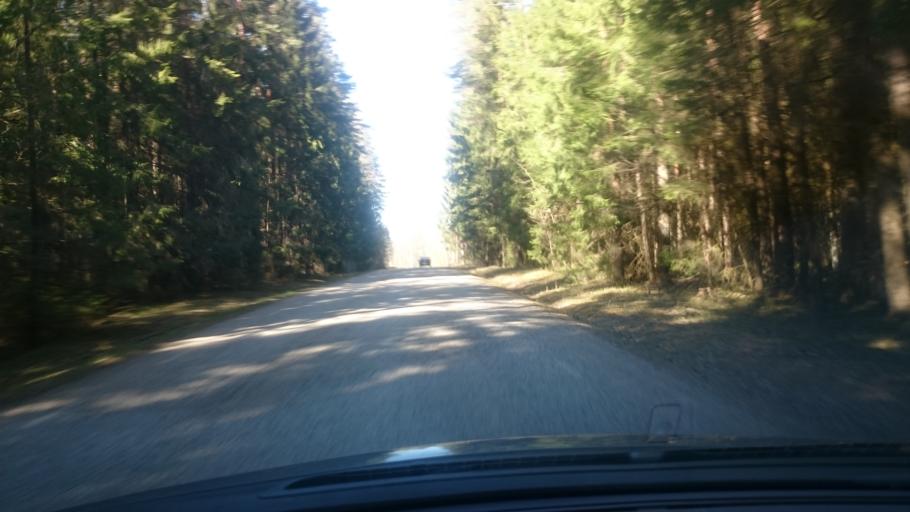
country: EE
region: Polvamaa
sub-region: Polva linn
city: Polva
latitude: 58.1309
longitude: 27.0166
